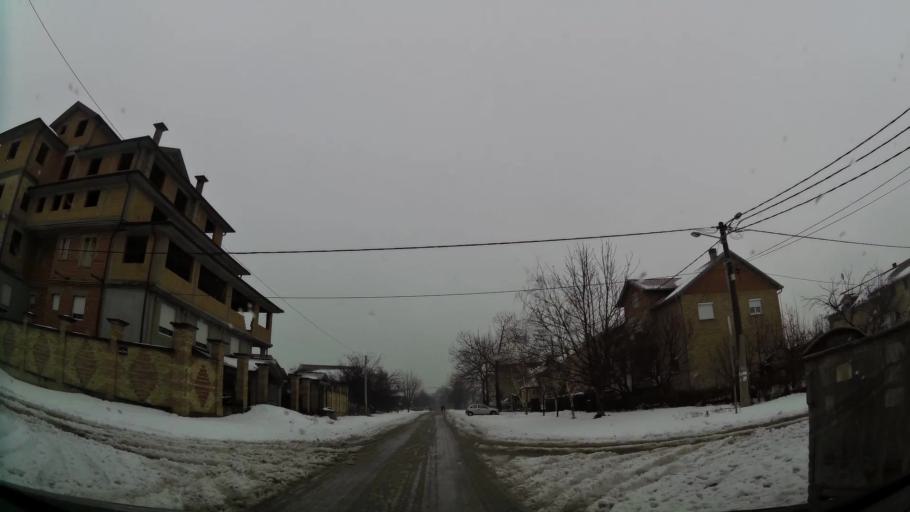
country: RS
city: Novi Banovci
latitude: 44.8780
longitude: 20.3155
